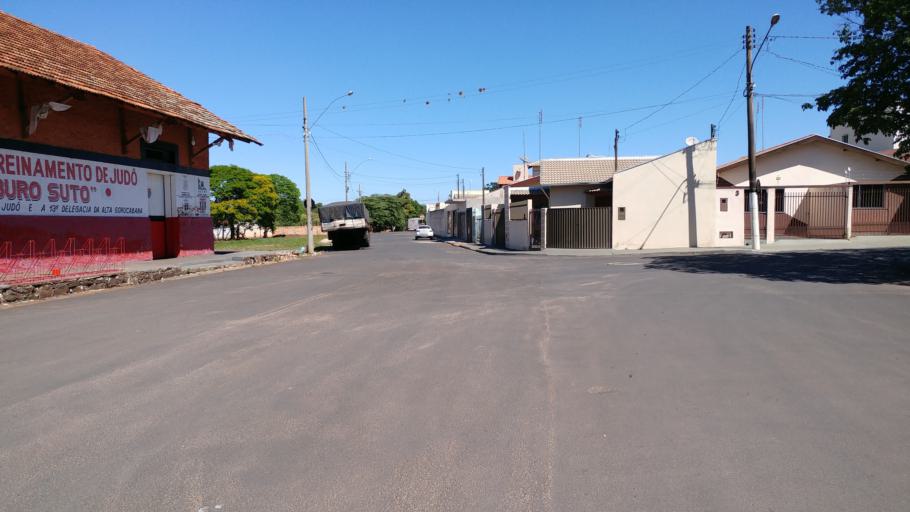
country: BR
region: Sao Paulo
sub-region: Paraguacu Paulista
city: Paraguacu Paulista
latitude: -22.4164
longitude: -50.5735
